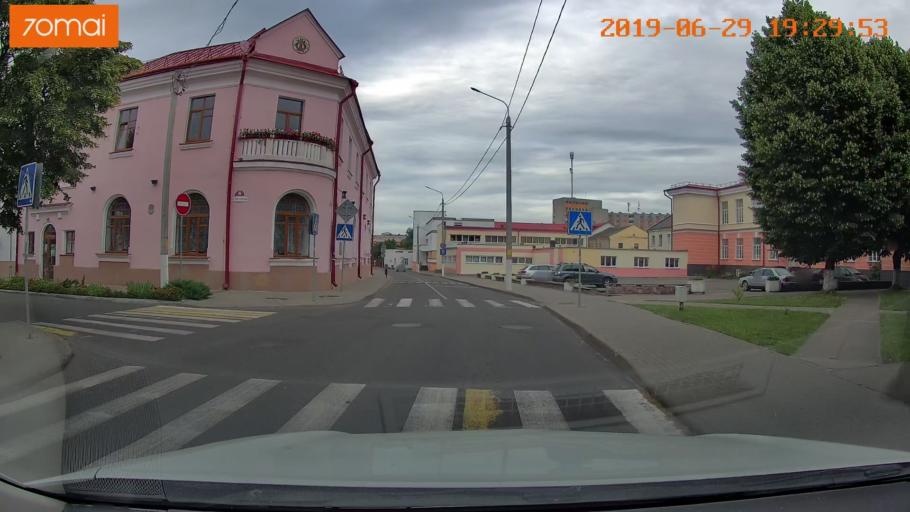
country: BY
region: Brest
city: Pinsk
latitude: 52.1145
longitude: 26.1104
